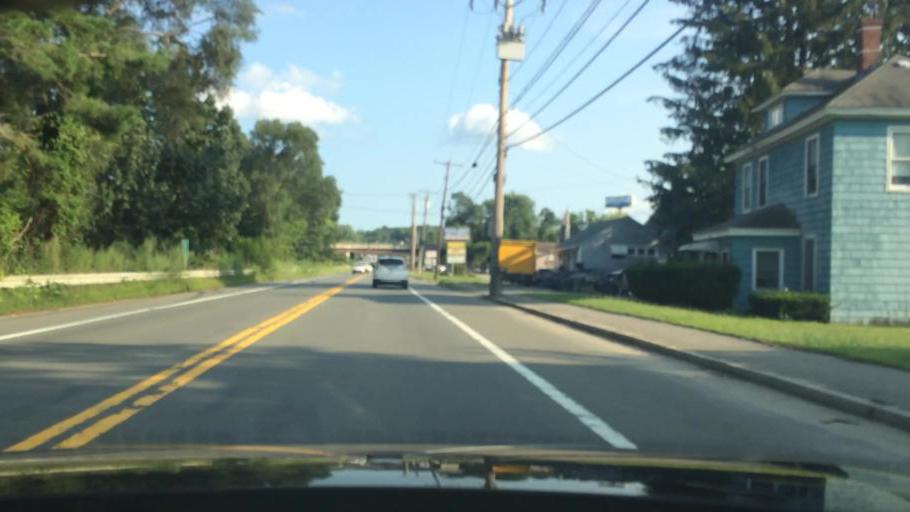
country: US
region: Massachusetts
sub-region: Essex County
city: Haverhill
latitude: 42.7554
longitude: -71.1302
